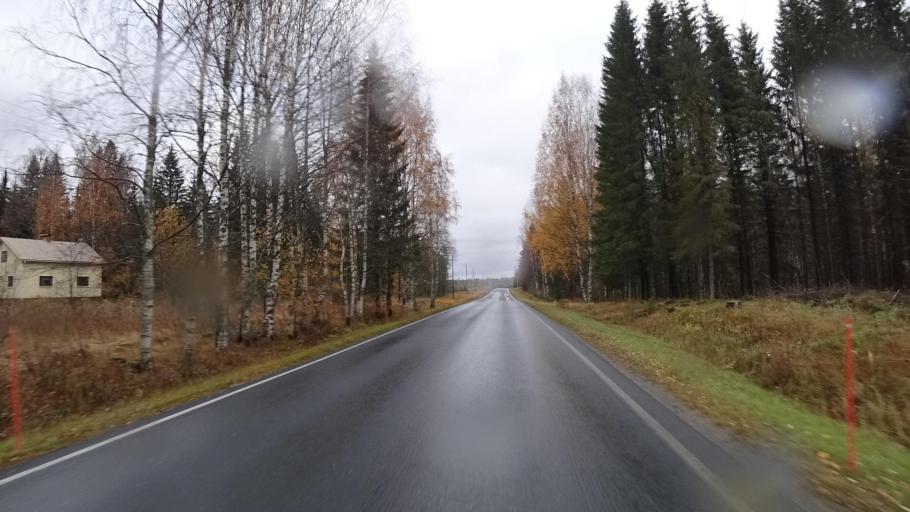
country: FI
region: North Karelia
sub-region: Joensuu
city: Polvijaervi
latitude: 63.0802
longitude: 29.5764
